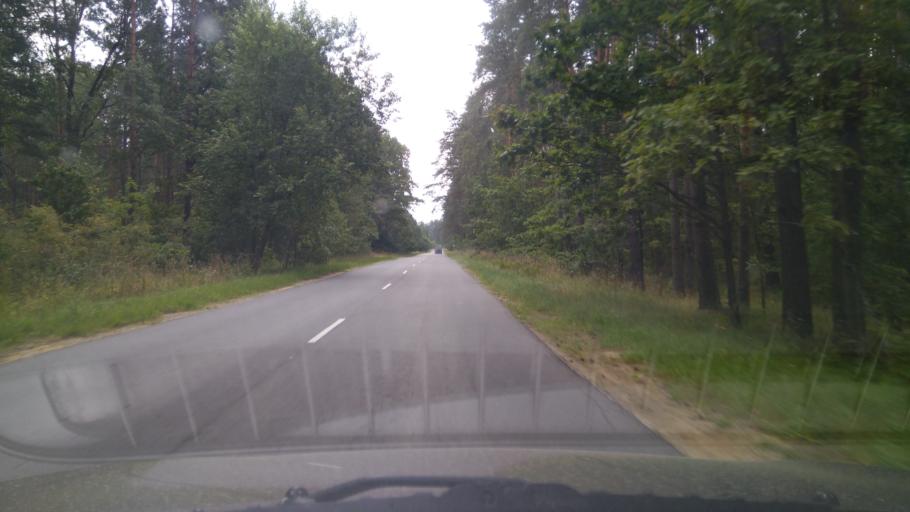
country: BY
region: Brest
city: Nyakhachava
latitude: 52.5978
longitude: 25.1008
